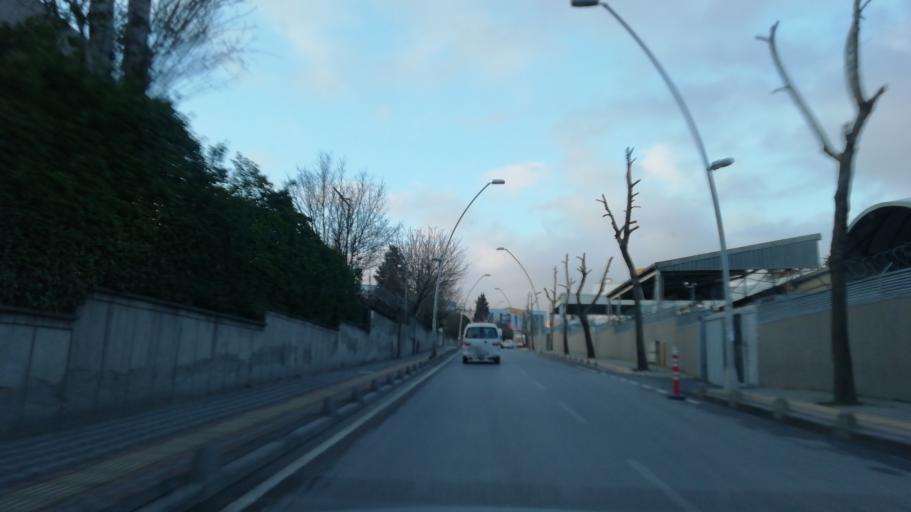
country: TR
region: Istanbul
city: Bahcelievler
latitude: 41.0036
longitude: 28.8216
